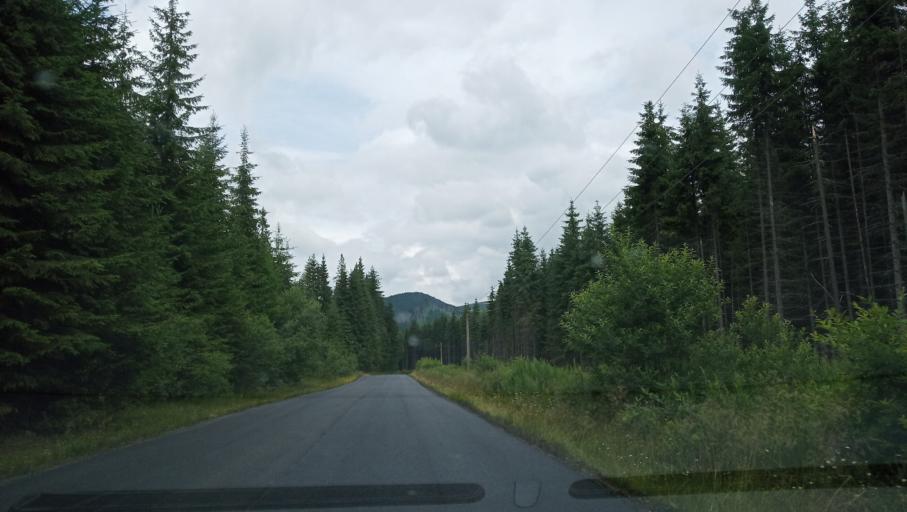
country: RO
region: Gorj
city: Novaci-Straini
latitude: 45.4222
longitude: 23.6959
